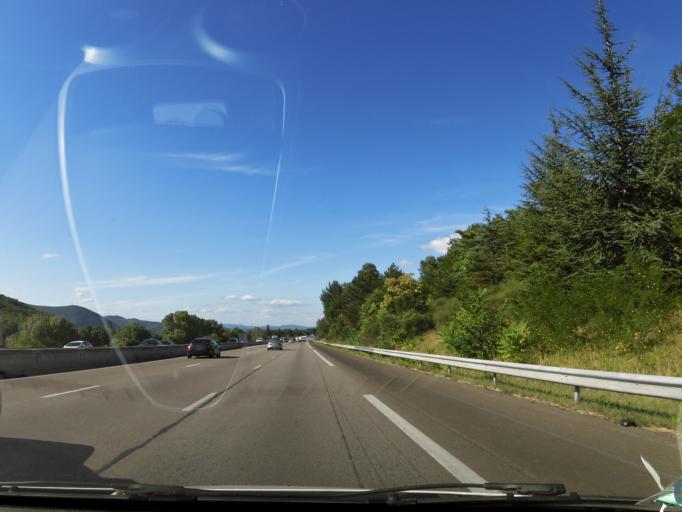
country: FR
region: Rhone-Alpes
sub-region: Departement de la Drome
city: Savasse
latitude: 44.6350
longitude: 4.7923
